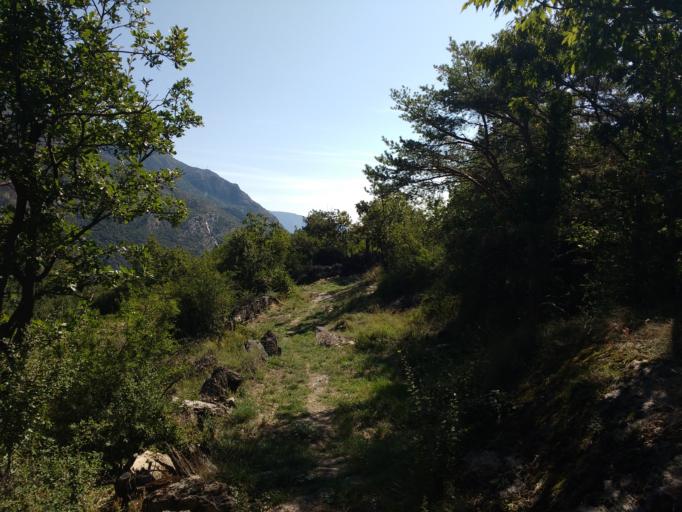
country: IT
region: Piedmont
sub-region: Provincia di Torino
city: Giaglione
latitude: 45.1435
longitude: 7.0283
